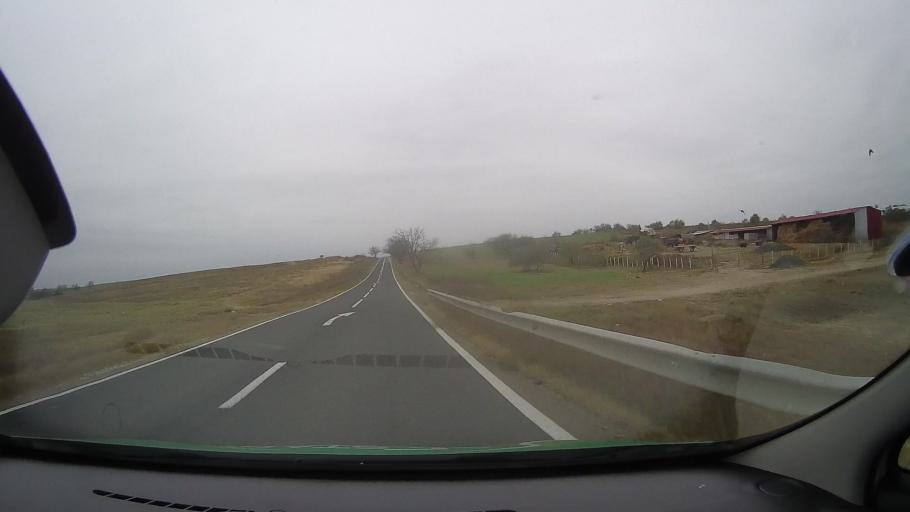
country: RO
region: Constanta
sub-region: Comuna Ghindaresti
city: Ghindaresti
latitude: 44.7064
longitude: 28.0541
